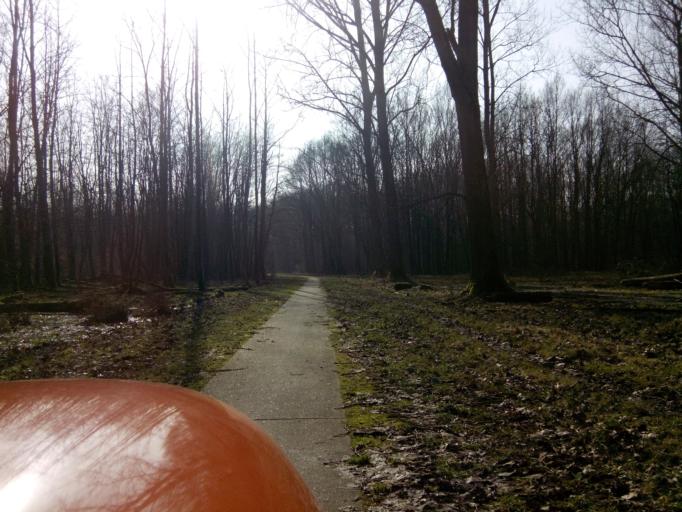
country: NL
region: Utrecht
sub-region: Gemeente Bunschoten
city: Bunschoten
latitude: 52.2611
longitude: 5.4167
